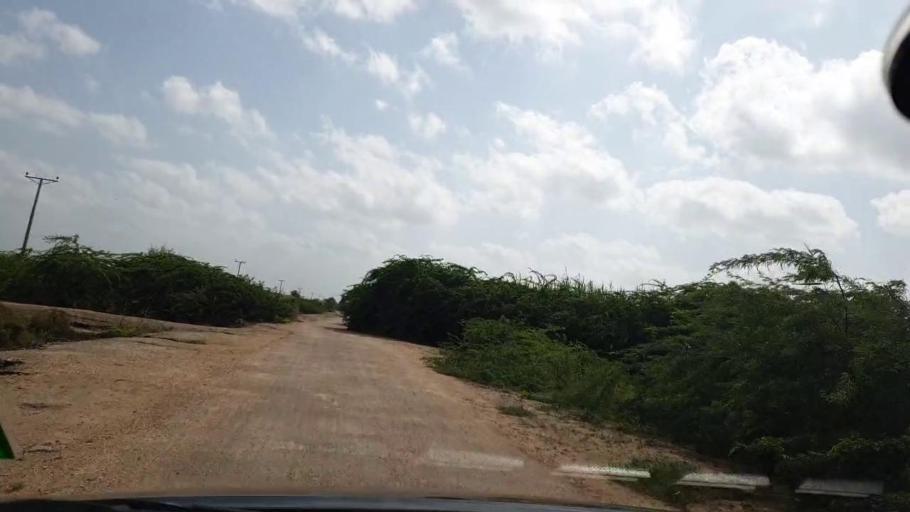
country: PK
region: Sindh
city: Kadhan
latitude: 24.5828
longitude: 69.1171
